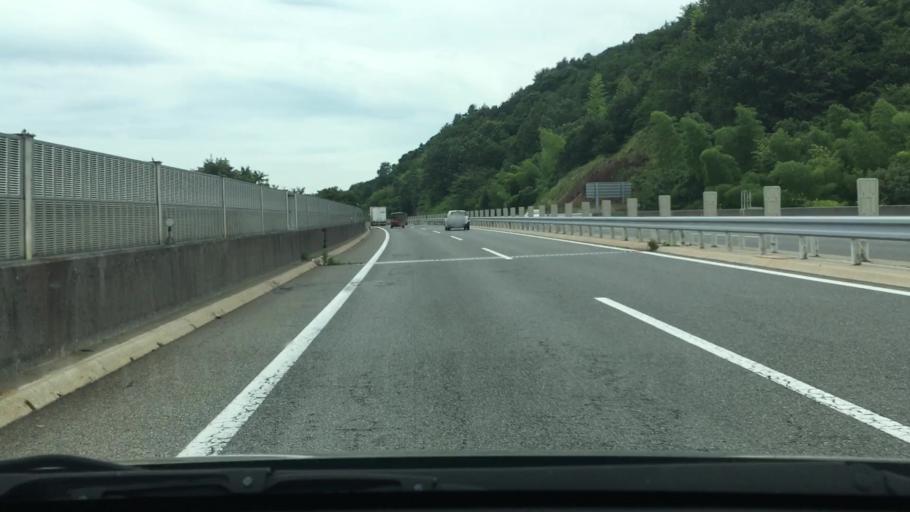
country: JP
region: Hiroshima
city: Ono-hara
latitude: 34.2848
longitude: 132.2620
